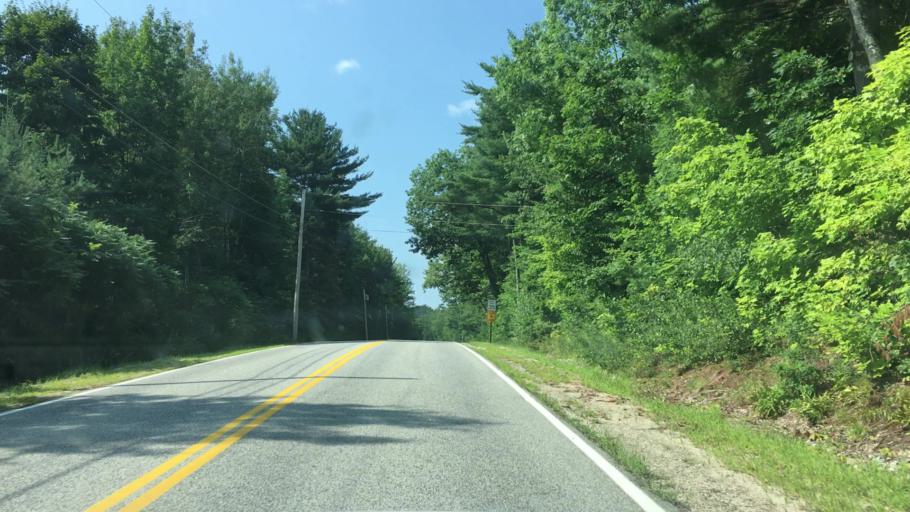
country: US
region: Maine
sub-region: Androscoggin County
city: Poland
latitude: 43.9798
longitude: -70.4020
